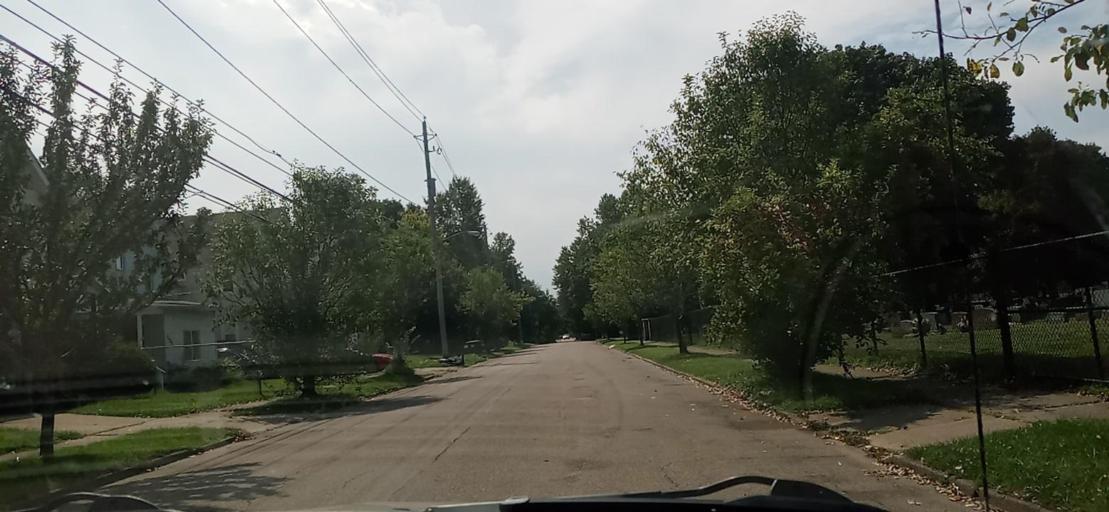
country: US
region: Ohio
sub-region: Summit County
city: Akron
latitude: 41.0499
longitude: -81.5250
